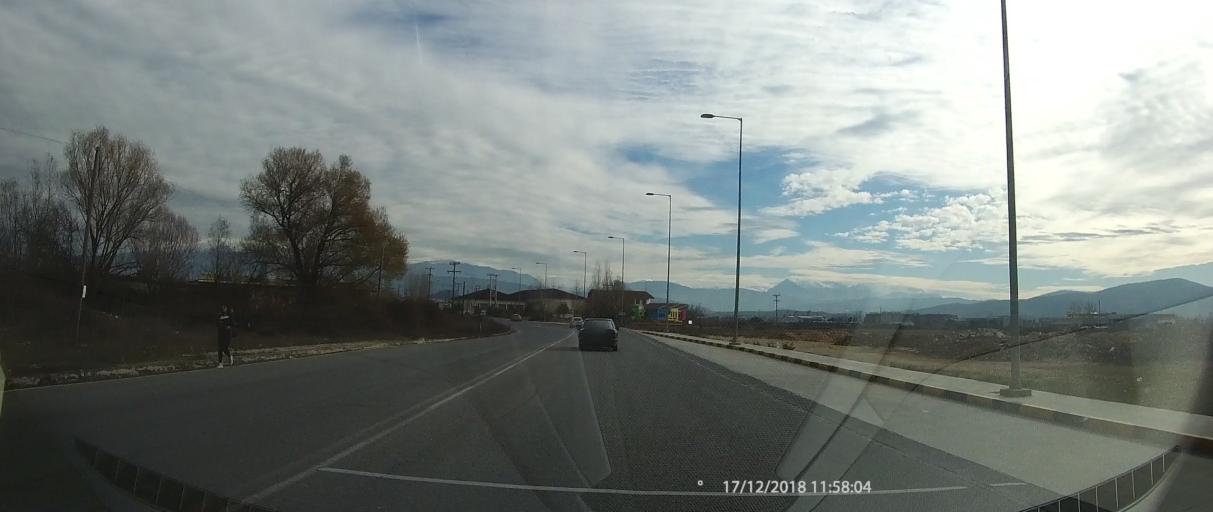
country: GR
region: Epirus
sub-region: Nomos Ioanninon
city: Anatoli
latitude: 39.6221
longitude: 20.8555
